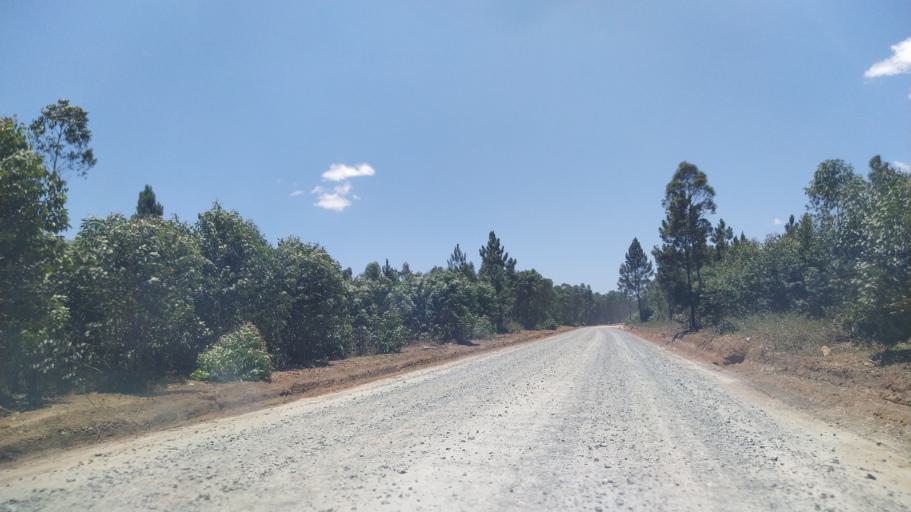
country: MG
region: Analamanga
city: Anjozorobe
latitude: -18.5328
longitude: 48.2582
